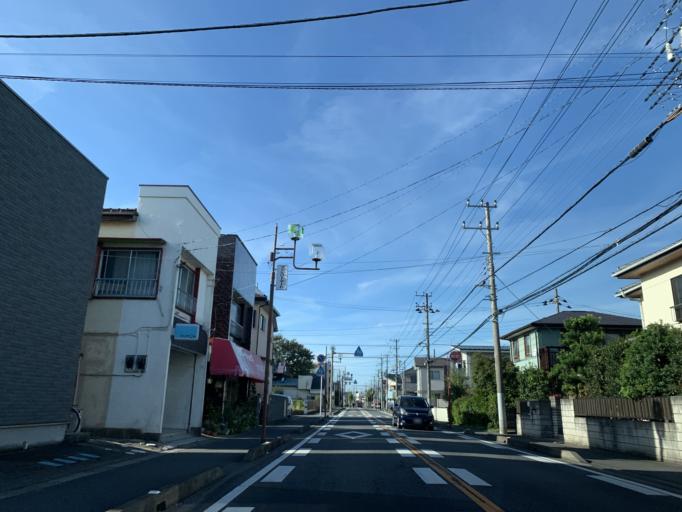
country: JP
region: Chiba
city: Nagareyama
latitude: 35.8837
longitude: 139.9229
